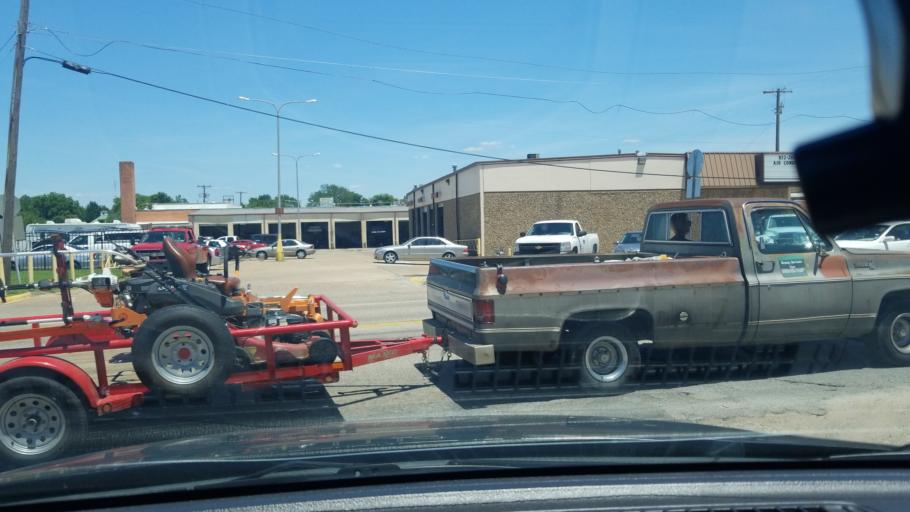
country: US
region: Texas
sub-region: Dallas County
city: Mesquite
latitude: 32.7671
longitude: -96.5993
